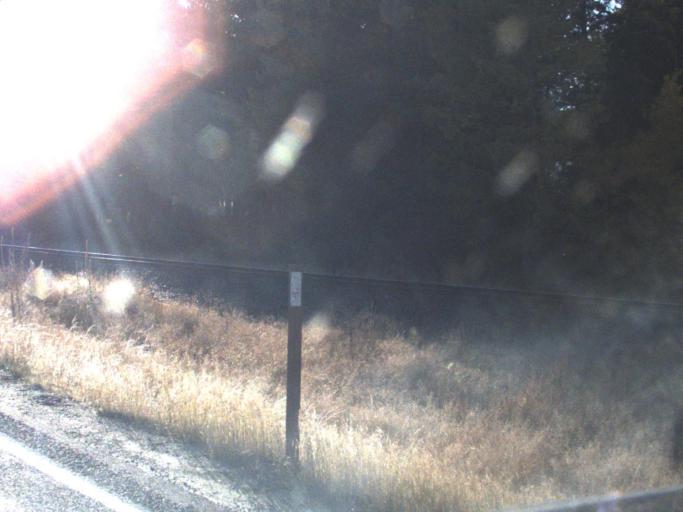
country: US
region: Washington
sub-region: Stevens County
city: Kettle Falls
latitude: 48.8247
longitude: -117.9140
